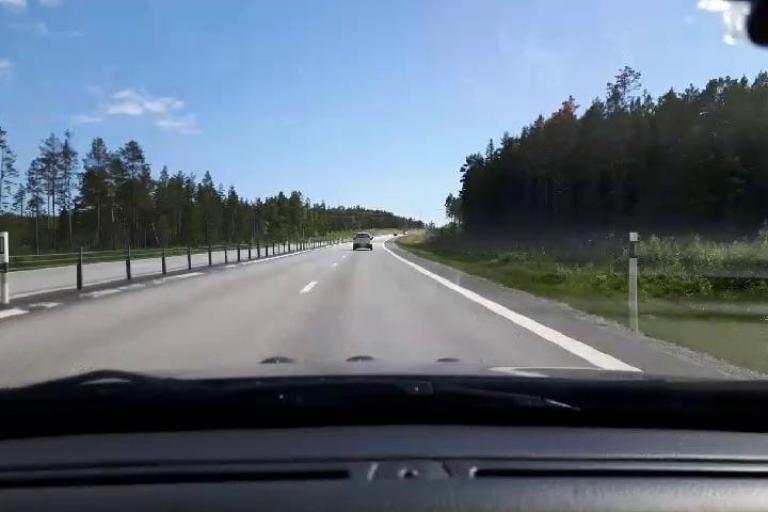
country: SE
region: Gaevleborg
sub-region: Hudiksvalls Kommun
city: Hudiksvall
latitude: 61.6993
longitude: 17.0557
